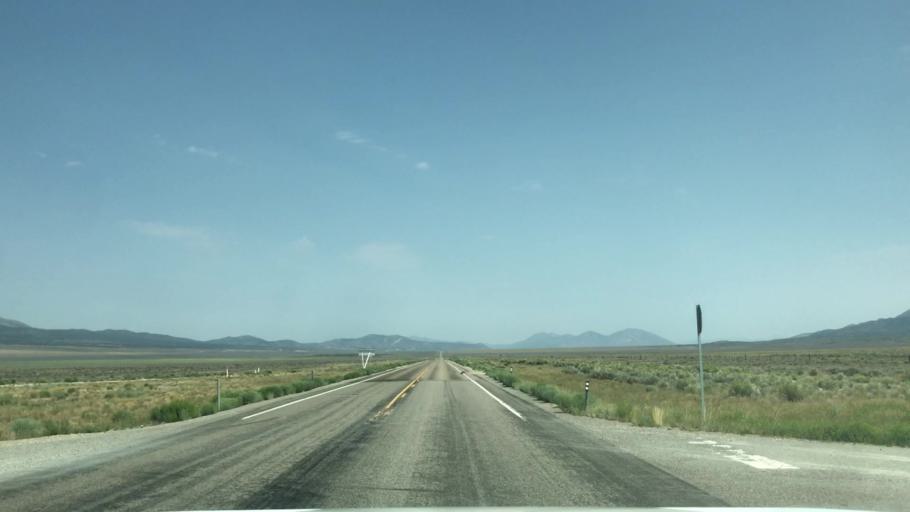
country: US
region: Nevada
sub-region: White Pine County
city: Ely
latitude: 39.0885
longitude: -114.7518
